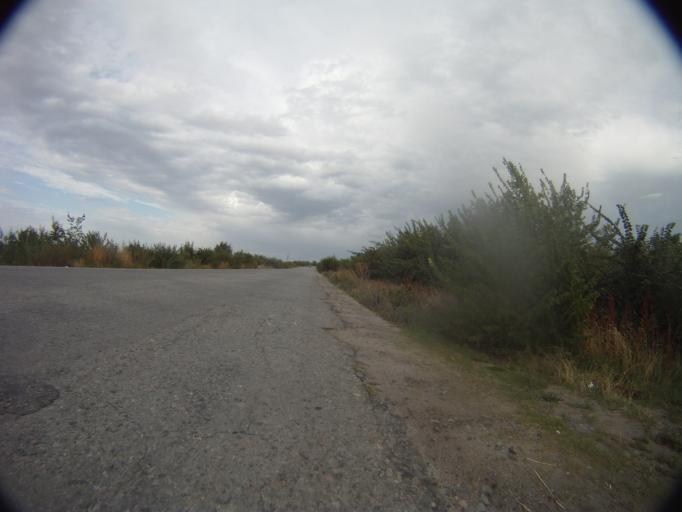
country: KG
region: Ysyk-Koel
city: Pokrovka
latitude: 42.2967
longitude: 77.8358
